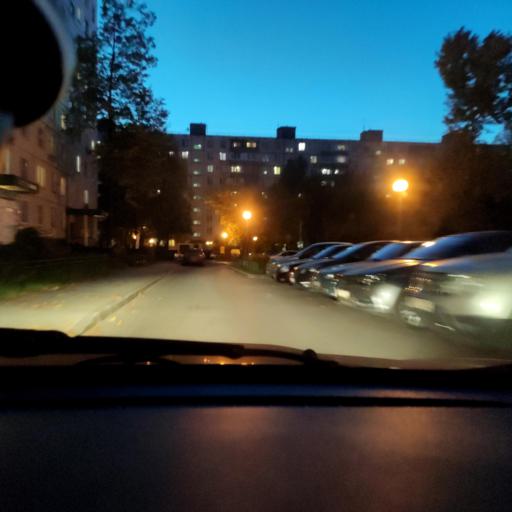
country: RU
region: Samara
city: Tol'yatti
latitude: 53.5082
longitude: 49.2805
